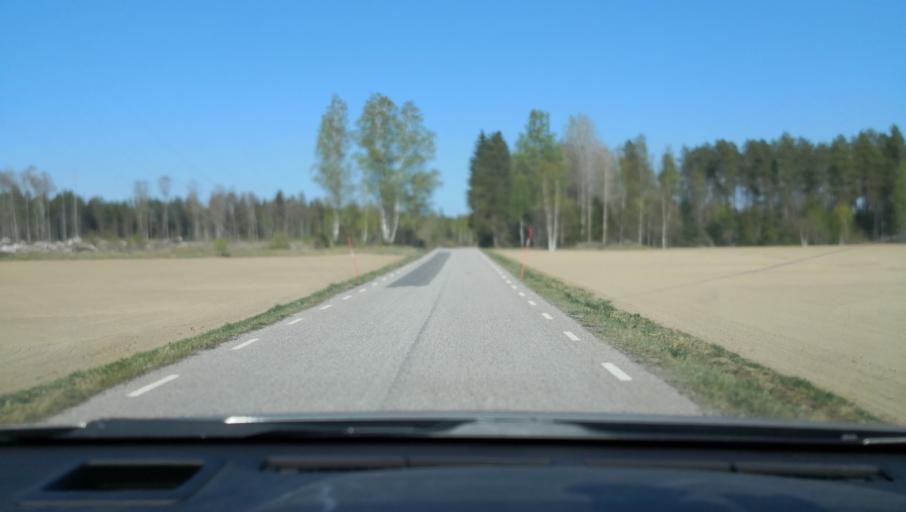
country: SE
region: Uppsala
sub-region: Heby Kommun
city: Heby
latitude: 60.0414
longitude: 16.8350
